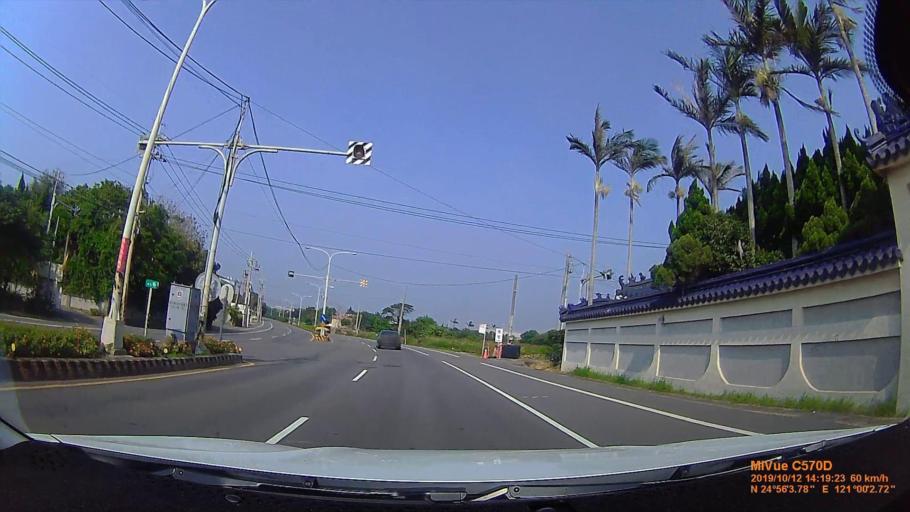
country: TW
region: Taiwan
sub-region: Hsinchu
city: Zhubei
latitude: 24.9345
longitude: 121.0009
